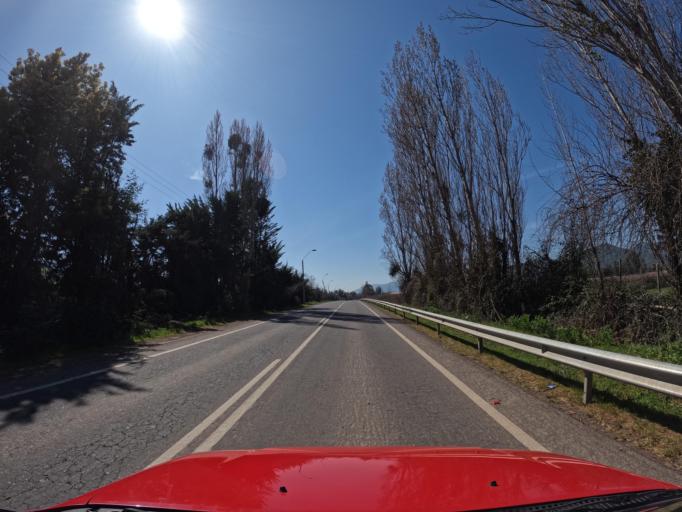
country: CL
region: Maule
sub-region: Provincia de Curico
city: Molina
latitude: -35.0532
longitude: -71.4797
